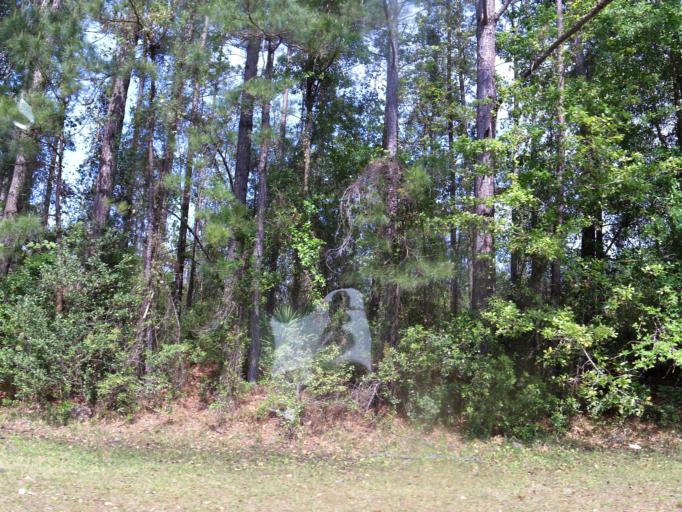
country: US
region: Georgia
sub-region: Camden County
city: Kingsland
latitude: 30.8083
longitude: -81.7507
